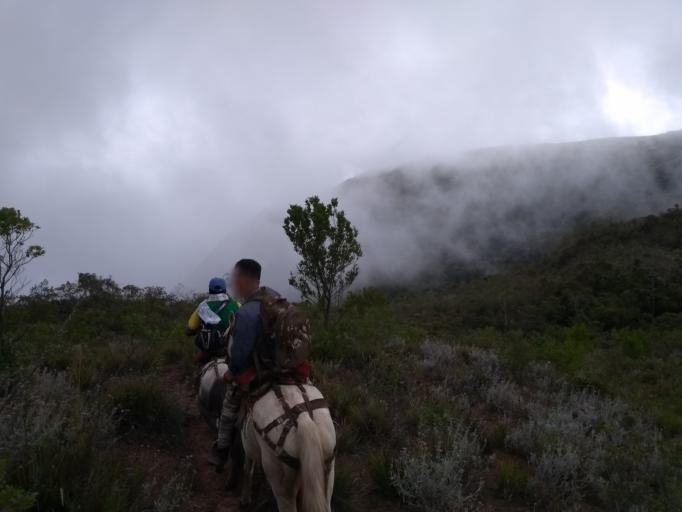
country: CO
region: Cesar
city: Manaure Balcon del Cesar
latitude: 10.2154
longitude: -73.0114
